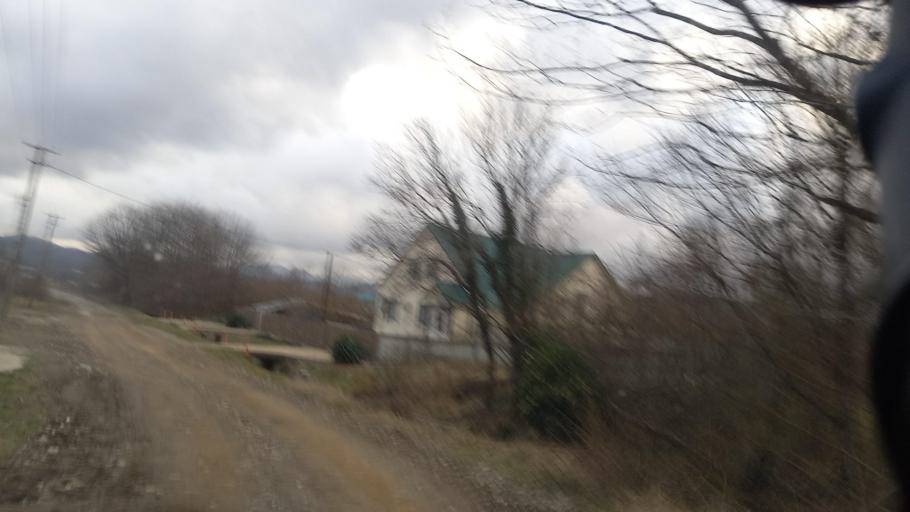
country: RU
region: Krasnodarskiy
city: Lermontovo
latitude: 44.4322
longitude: 38.7961
